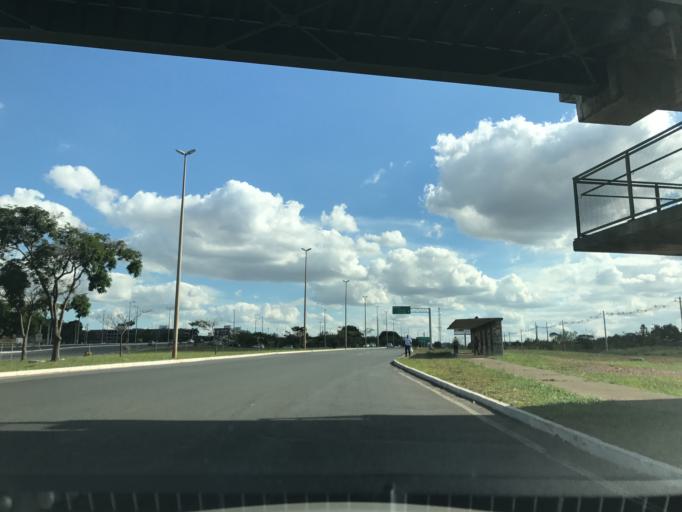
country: BR
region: Federal District
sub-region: Brasilia
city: Brasilia
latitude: -15.8103
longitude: -47.9768
